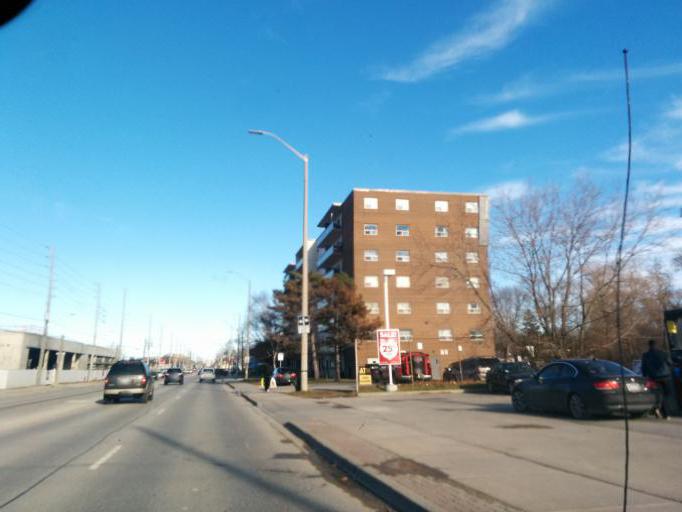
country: CA
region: Ontario
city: Mississauga
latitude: 43.5651
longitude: -79.5712
